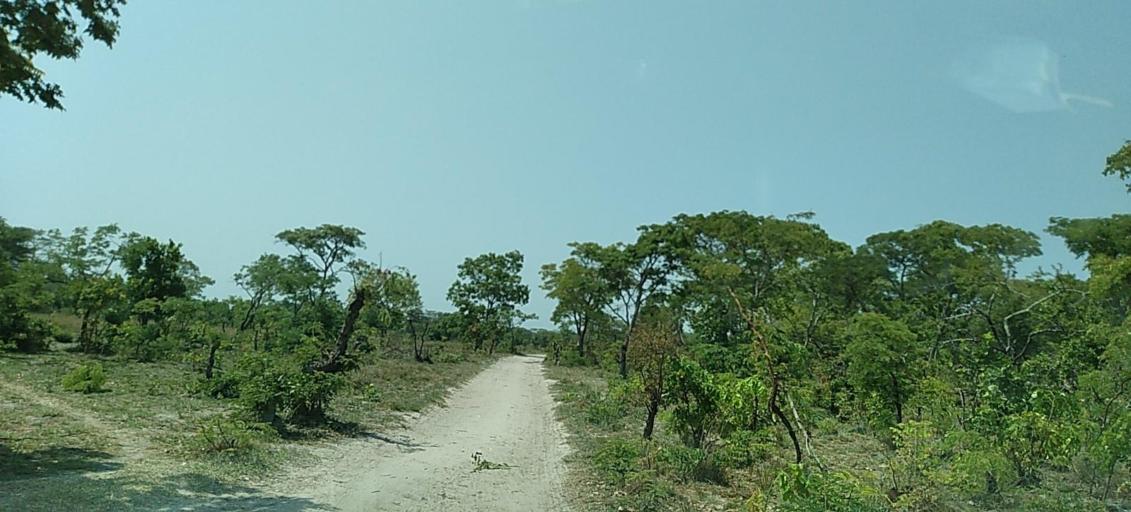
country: ZM
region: Copperbelt
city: Mpongwe
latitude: -13.8508
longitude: 28.0581
